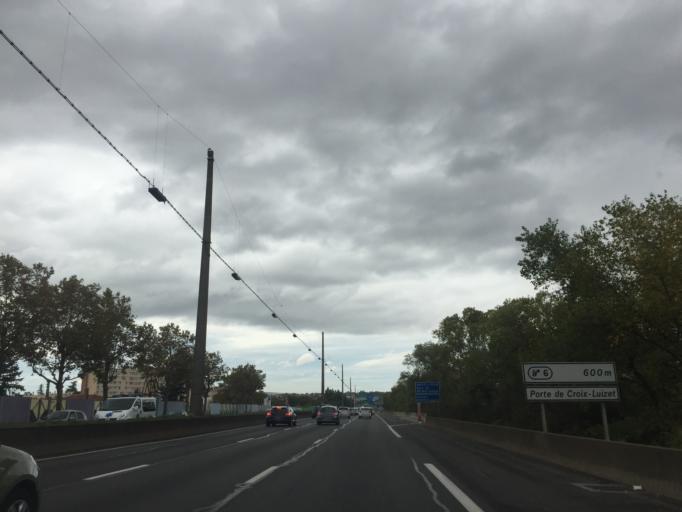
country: FR
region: Rhone-Alpes
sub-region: Departement du Rhone
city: Villeurbanne
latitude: 45.7749
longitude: 4.8988
